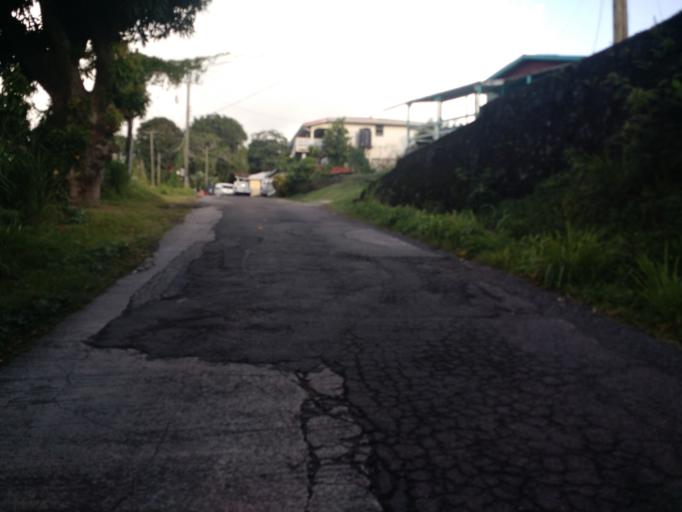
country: LC
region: Anse-la-Raye
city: Anse La Raye
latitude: 13.9625
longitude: -61.0215
